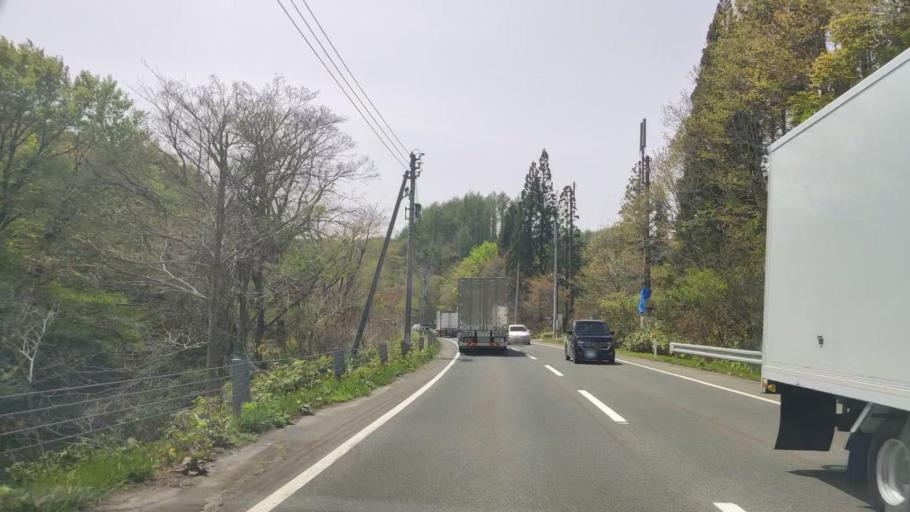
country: JP
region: Aomori
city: Aomori Shi
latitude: 40.7785
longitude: 141.0275
